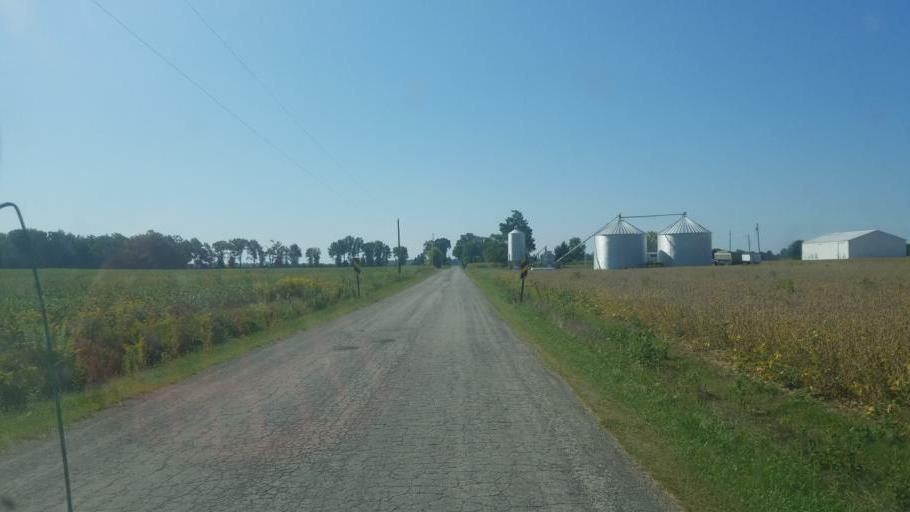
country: US
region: Ohio
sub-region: Morrow County
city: Cardington
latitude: 40.5844
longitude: -82.9382
